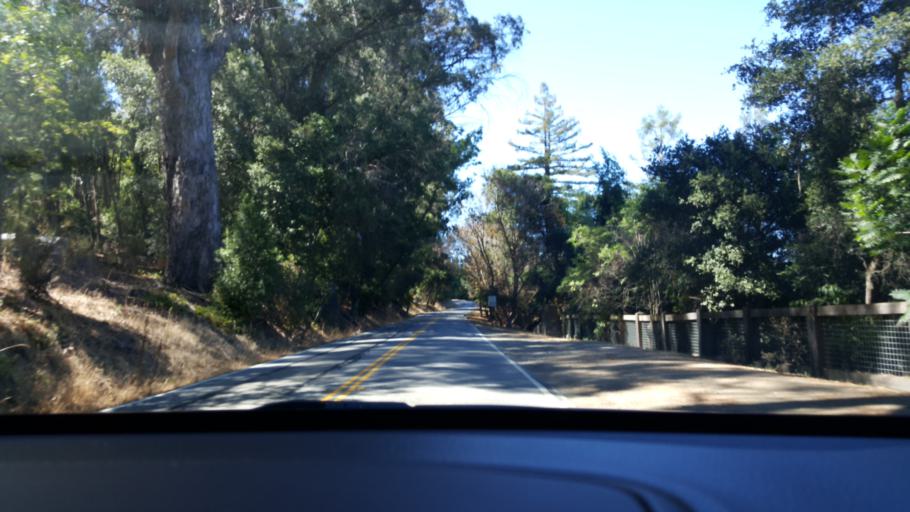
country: US
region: California
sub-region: San Mateo County
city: Woodside
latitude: 37.4045
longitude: -122.2553
